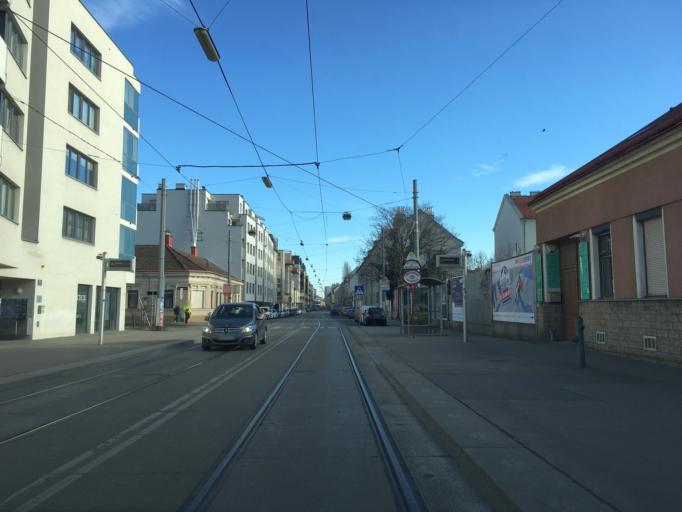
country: AT
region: Lower Austria
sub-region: Politischer Bezirk Wien-Umgebung
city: Gerasdorf bei Wien
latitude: 48.2506
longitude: 16.4357
